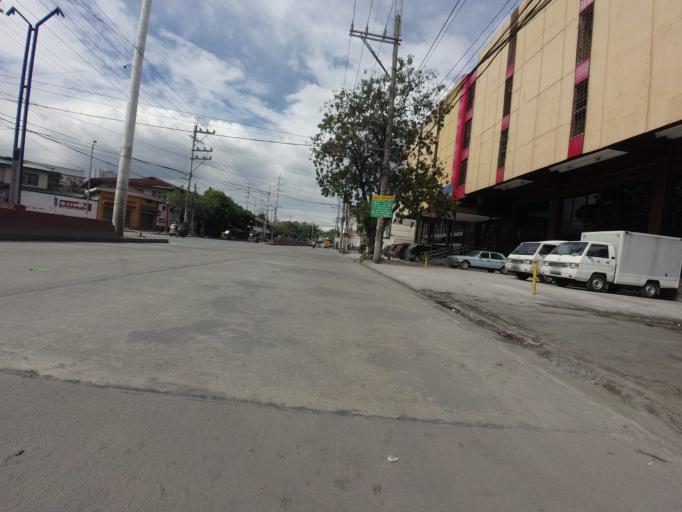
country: PH
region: Metro Manila
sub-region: City of Manila
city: Quiapo
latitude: 14.5846
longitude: 120.9950
